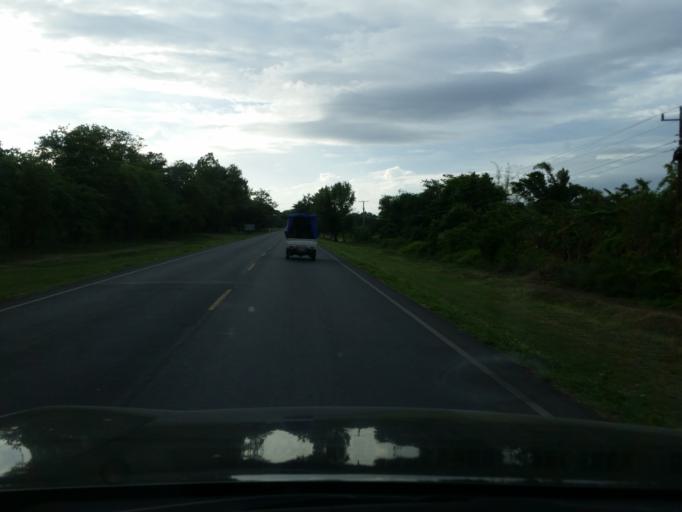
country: NI
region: Rivas
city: Belen
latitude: 11.5129
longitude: -85.8872
